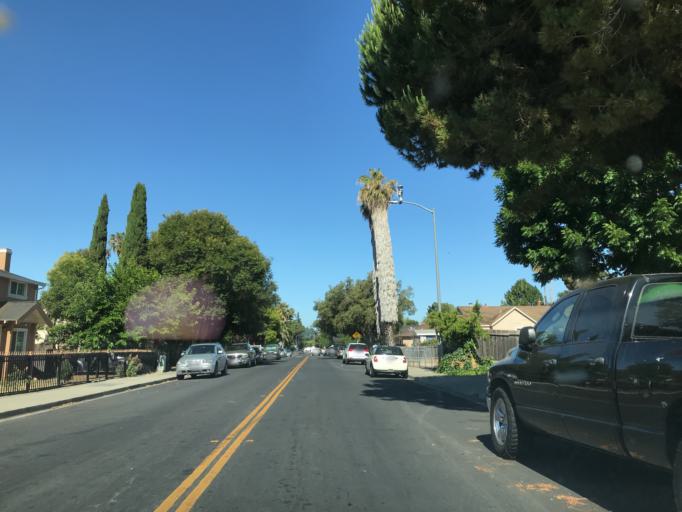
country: US
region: California
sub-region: San Mateo County
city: East Palo Alto
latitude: 37.4662
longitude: -122.1350
